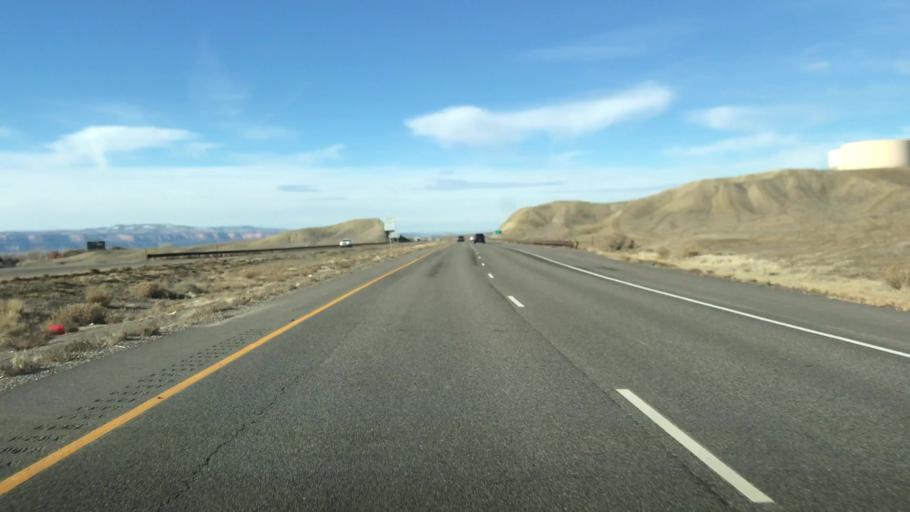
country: US
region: Colorado
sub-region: Mesa County
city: Clifton
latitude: 39.1035
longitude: -108.4552
